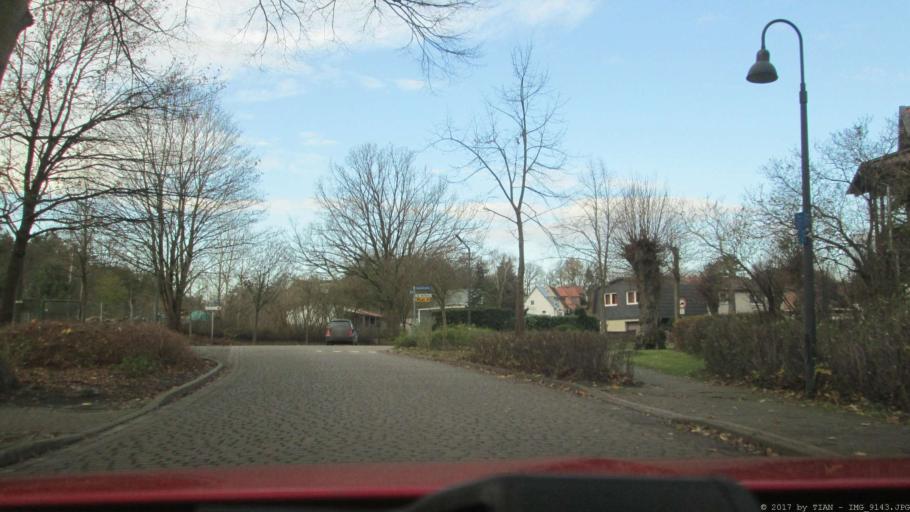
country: DE
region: Lower Saxony
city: Hankensbuttel
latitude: 52.7260
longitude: 10.6101
